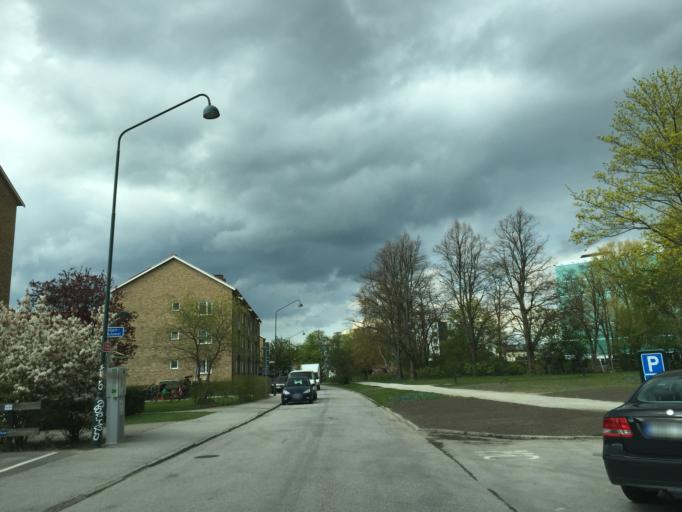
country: SE
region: Skane
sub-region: Lunds Kommun
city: Lund
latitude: 55.7071
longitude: 13.1843
